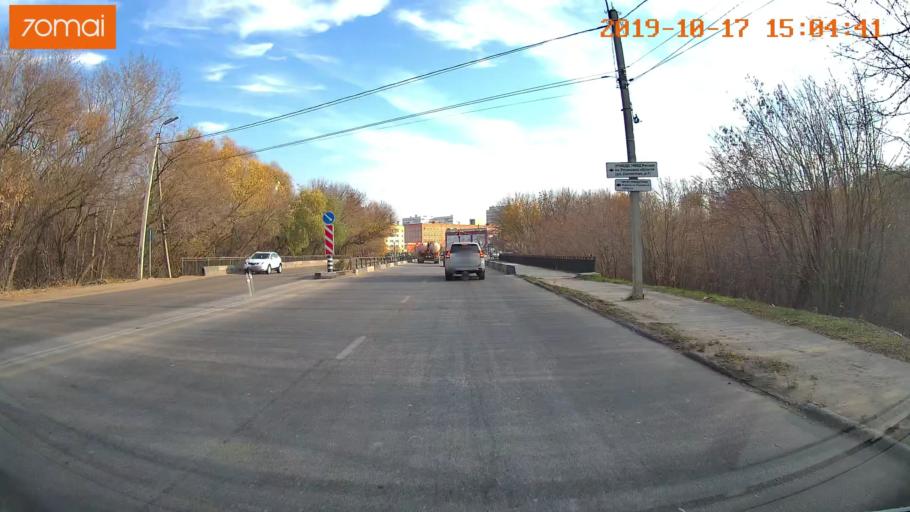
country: RU
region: Rjazan
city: Ryazan'
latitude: 54.6382
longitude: 39.7214
